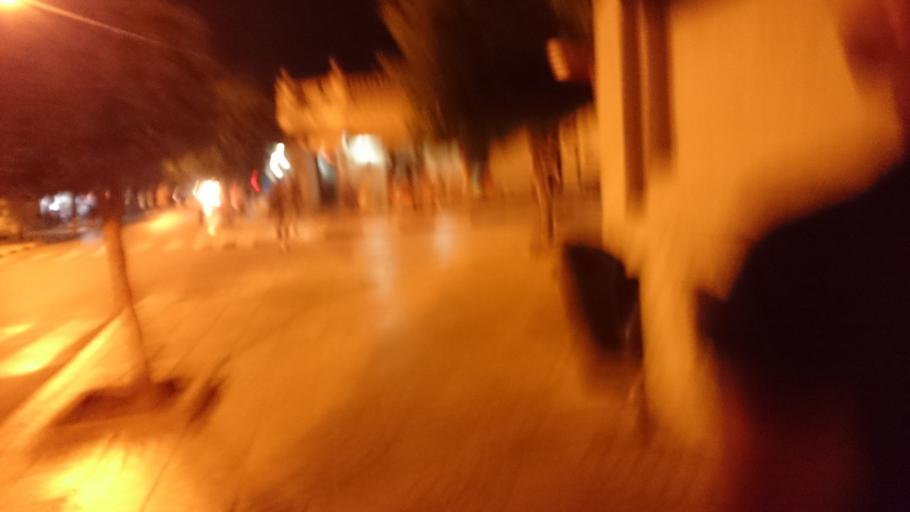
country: MA
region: Tanger-Tetouan
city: Asilah
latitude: 35.4671
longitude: -6.0325
